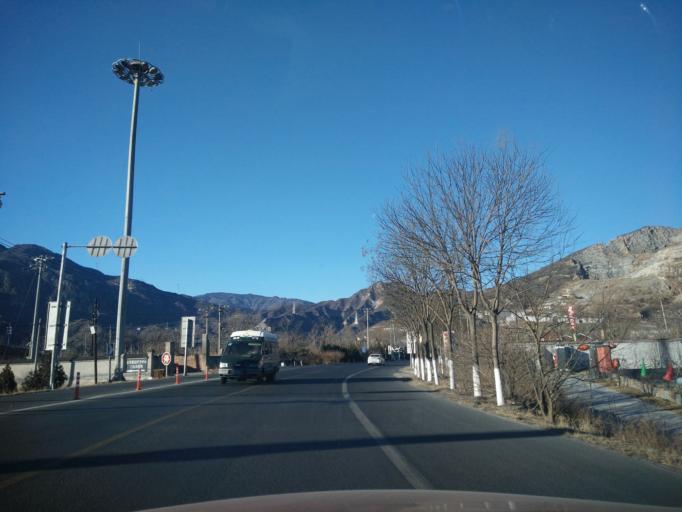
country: CN
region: Beijing
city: Miaofengshan
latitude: 39.9793
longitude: 116.0586
